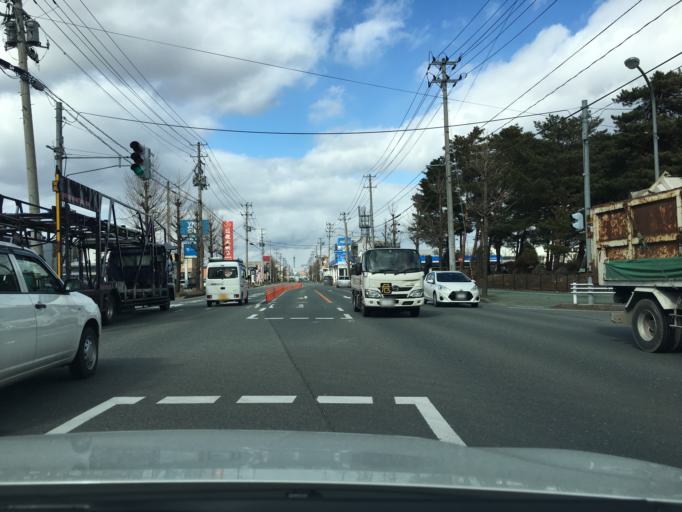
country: JP
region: Yamagata
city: Yamagata-shi
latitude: 38.2473
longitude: 140.3087
